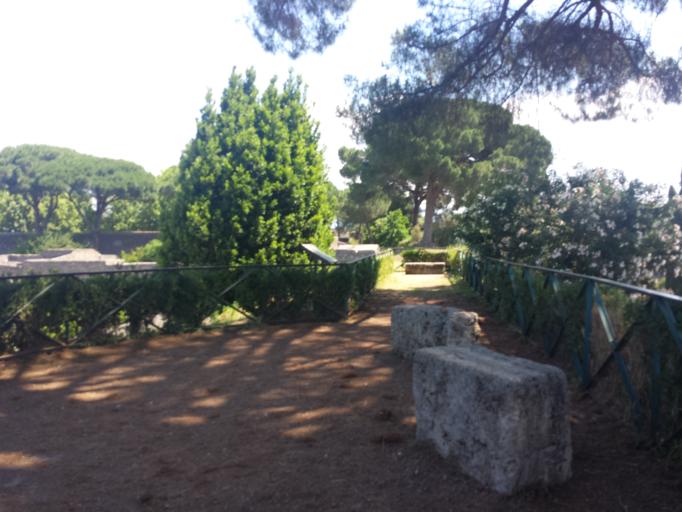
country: IT
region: Campania
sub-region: Provincia di Napoli
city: Pompei
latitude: 40.7493
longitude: 14.4929
